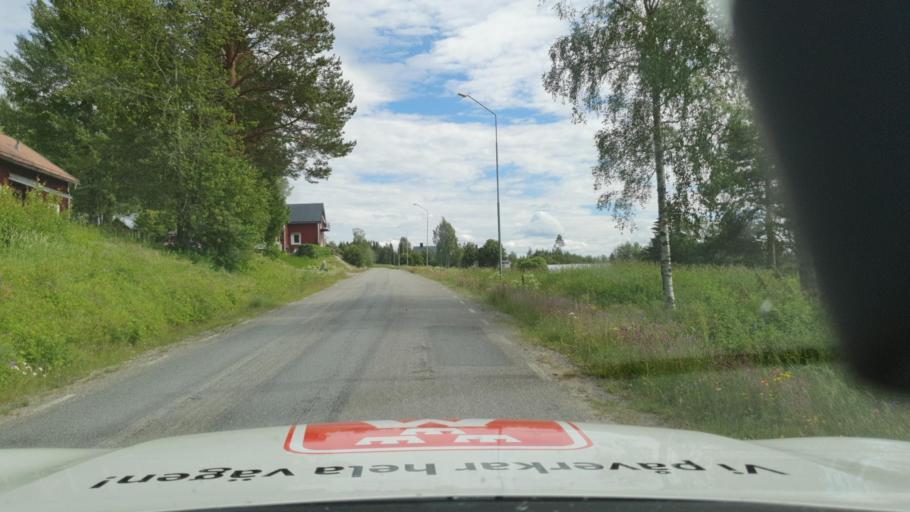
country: SE
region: Vaesterbotten
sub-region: Norsjo Kommun
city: Norsjoe
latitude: 64.8797
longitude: 19.4615
